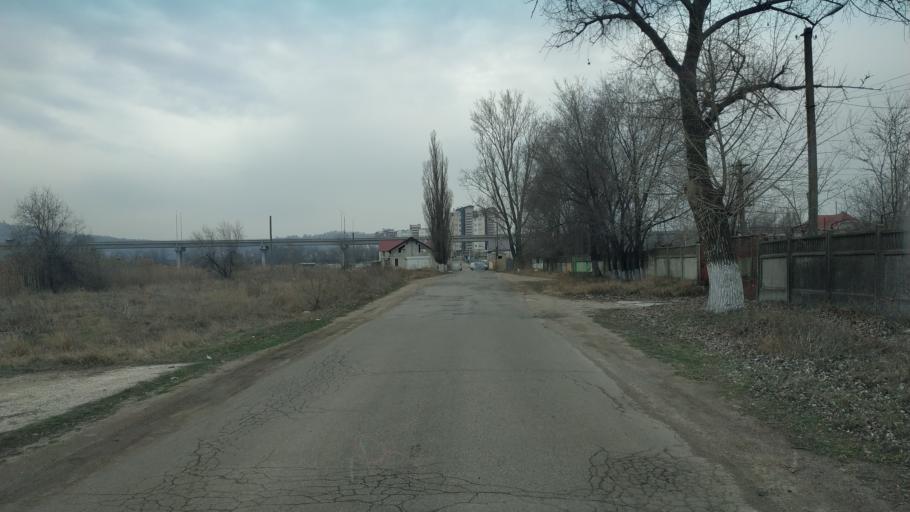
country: MD
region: Chisinau
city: Singera
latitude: 46.9220
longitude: 28.9747
